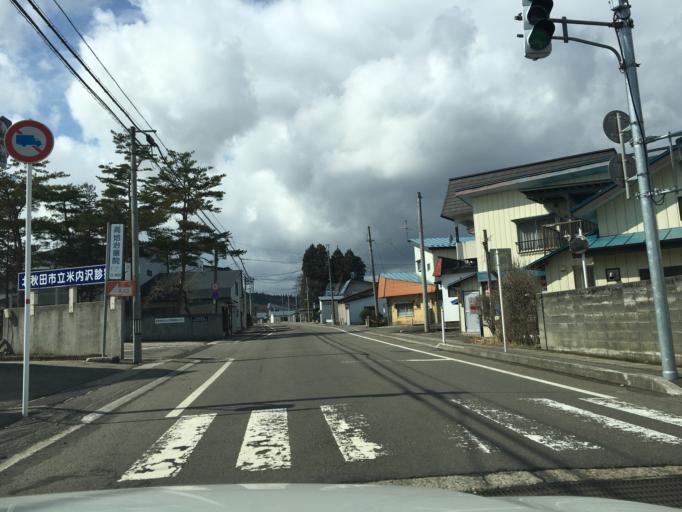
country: JP
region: Akita
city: Takanosu
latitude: 40.1197
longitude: 140.3752
